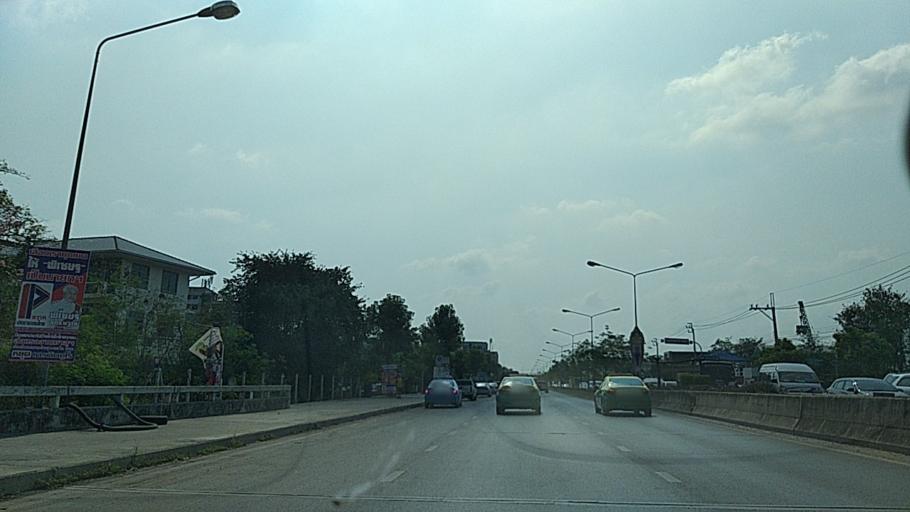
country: TH
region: Bangkok
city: Bang Khen
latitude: 13.8893
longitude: 100.6089
